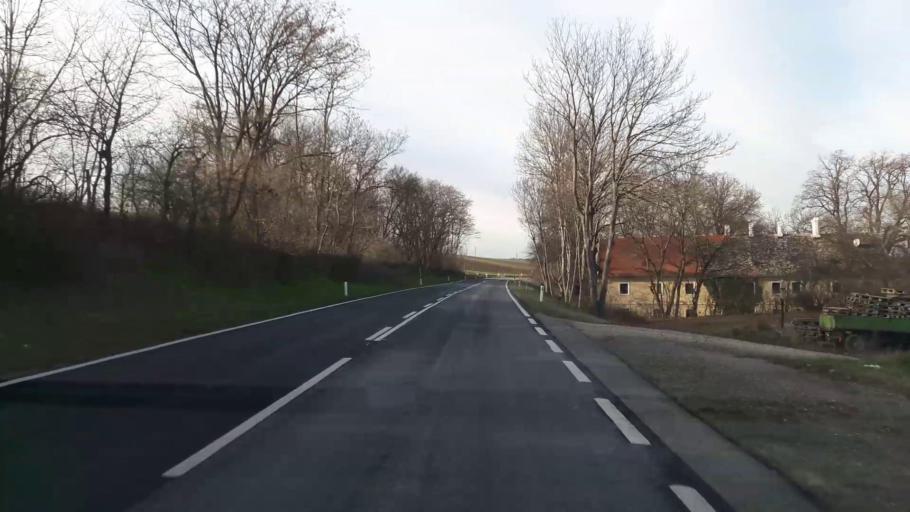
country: AT
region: Lower Austria
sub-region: Politischer Bezirk Ganserndorf
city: Gross-Schweinbarth
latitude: 48.4275
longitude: 16.6156
